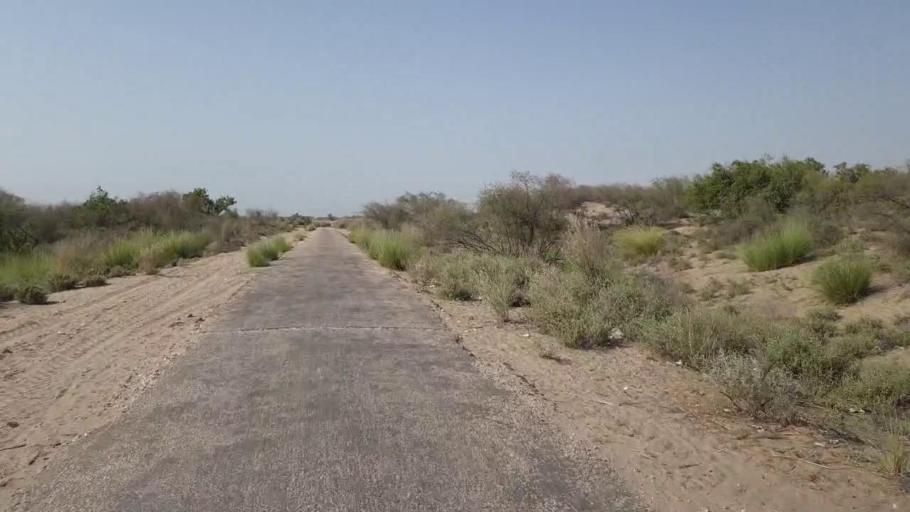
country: PK
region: Sindh
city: Jam Sahib
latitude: 26.5949
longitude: 68.9227
